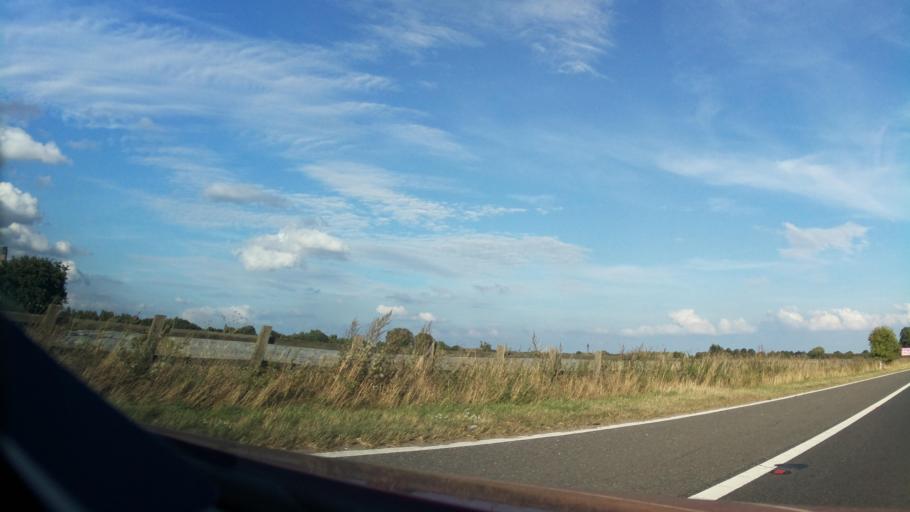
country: GB
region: England
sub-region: East Riding of Yorkshire
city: Pollington
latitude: 53.6951
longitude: -1.1331
